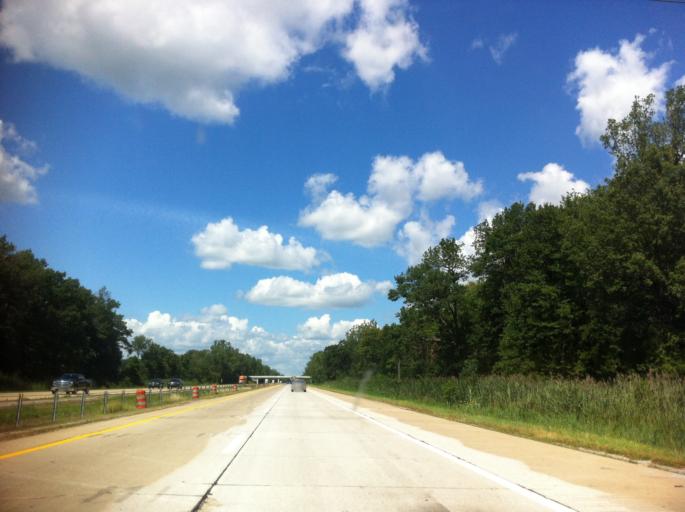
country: US
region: Michigan
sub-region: Monroe County
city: Petersburg
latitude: 41.8609
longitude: -83.6608
